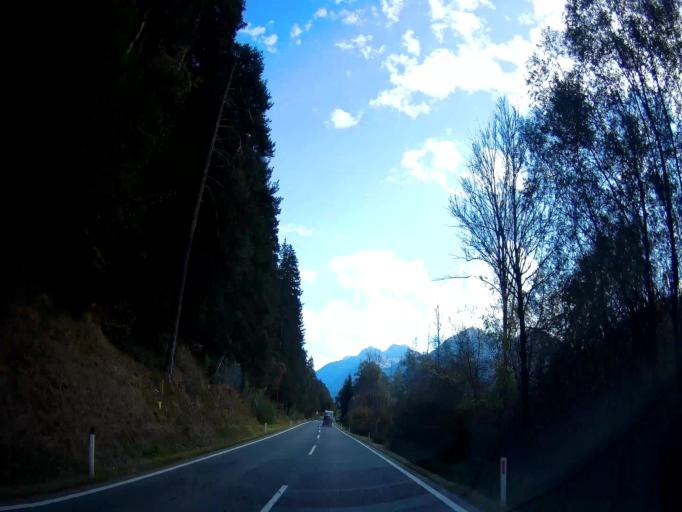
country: AT
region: Carinthia
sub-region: Politischer Bezirk Spittal an der Drau
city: Oberdrauburg
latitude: 46.7572
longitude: 12.9450
